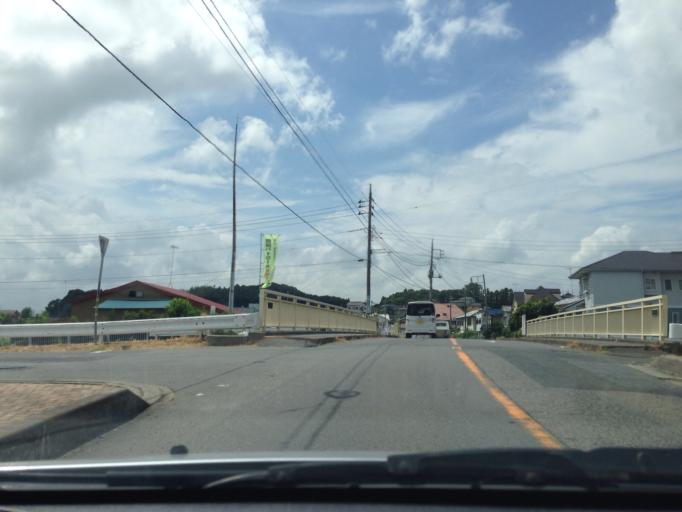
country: JP
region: Ibaraki
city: Ami
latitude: 36.0686
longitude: 140.2110
